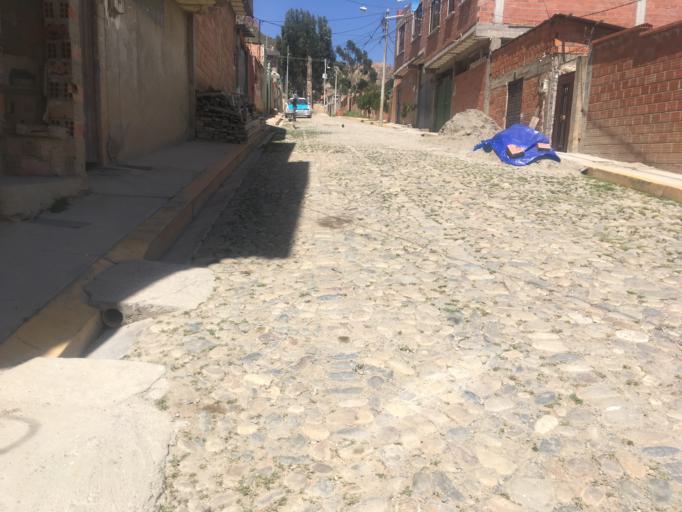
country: BO
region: La Paz
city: La Paz
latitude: -16.5436
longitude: -68.0440
